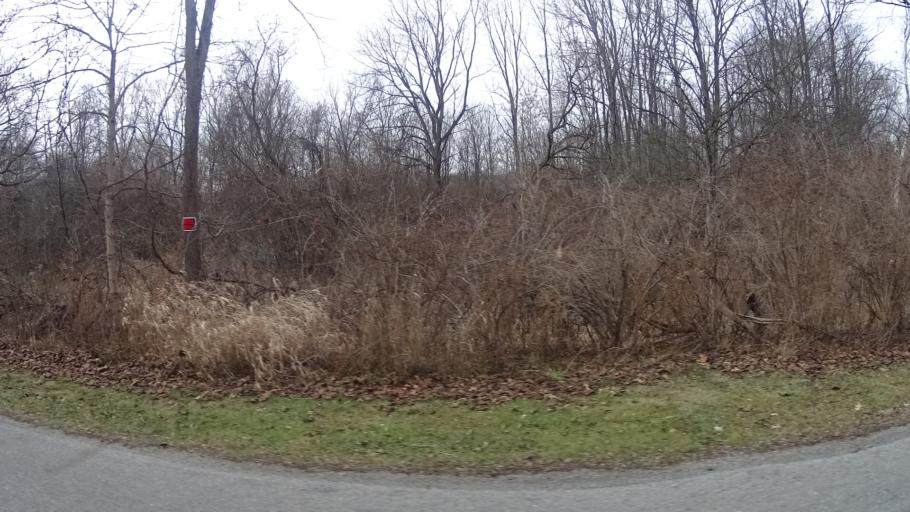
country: US
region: Ohio
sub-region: Lorain County
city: Wellington
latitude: 41.1721
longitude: -82.2426
